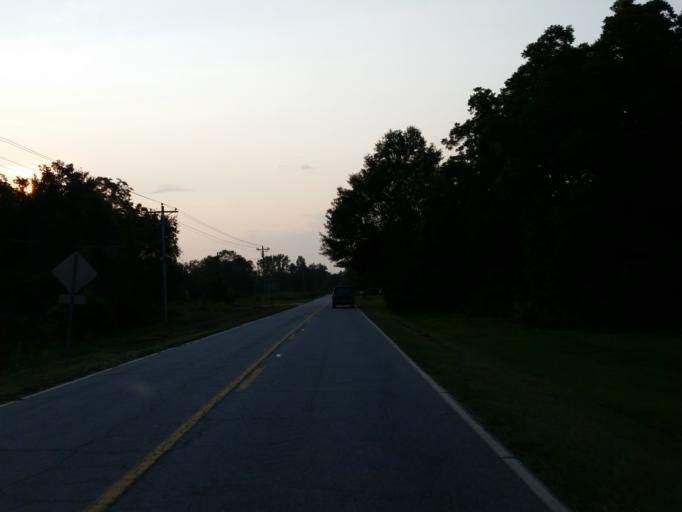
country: US
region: Georgia
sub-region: Henry County
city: Locust Grove
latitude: 33.2770
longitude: -84.1435
